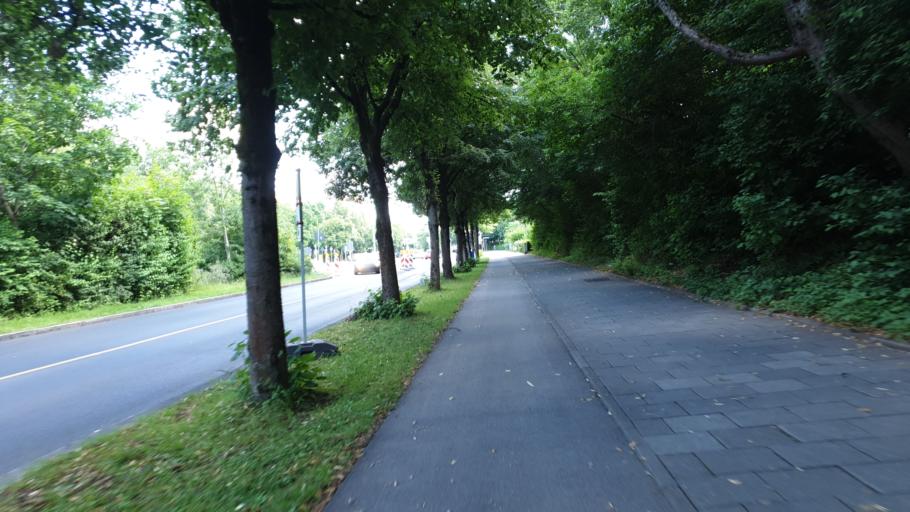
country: DE
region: Bavaria
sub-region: Upper Bavaria
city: Neubiberg
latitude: 48.1044
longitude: 11.6364
